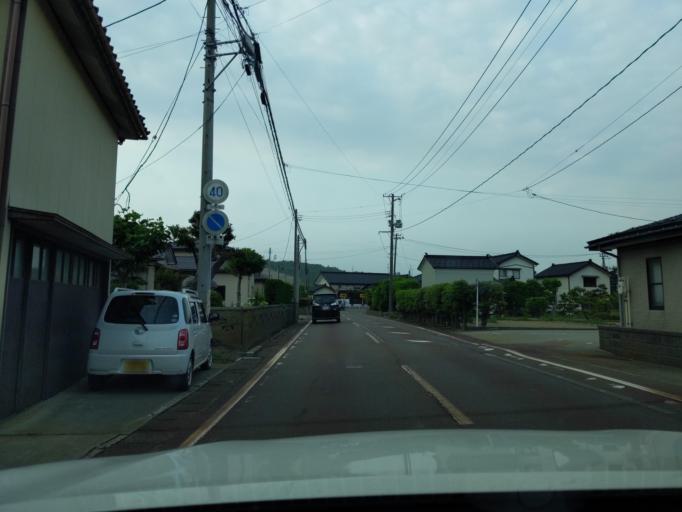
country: JP
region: Niigata
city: Kashiwazaki
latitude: 37.3892
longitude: 138.5856
